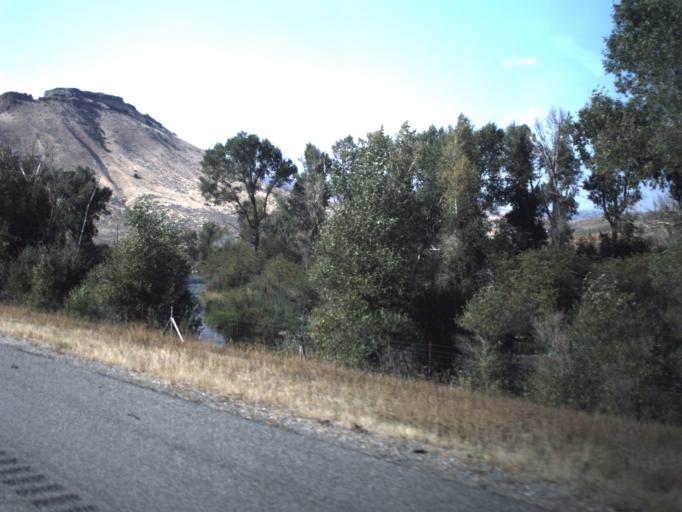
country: US
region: Utah
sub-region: Morgan County
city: Morgan
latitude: 41.0383
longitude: -111.5133
